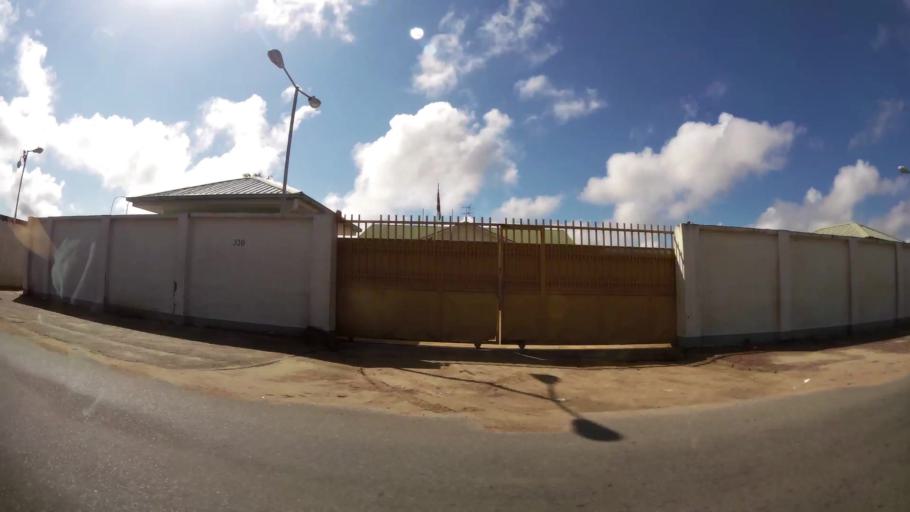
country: SR
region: Commewijne
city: Nieuw Amsterdam
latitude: 5.8544
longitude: -55.1052
